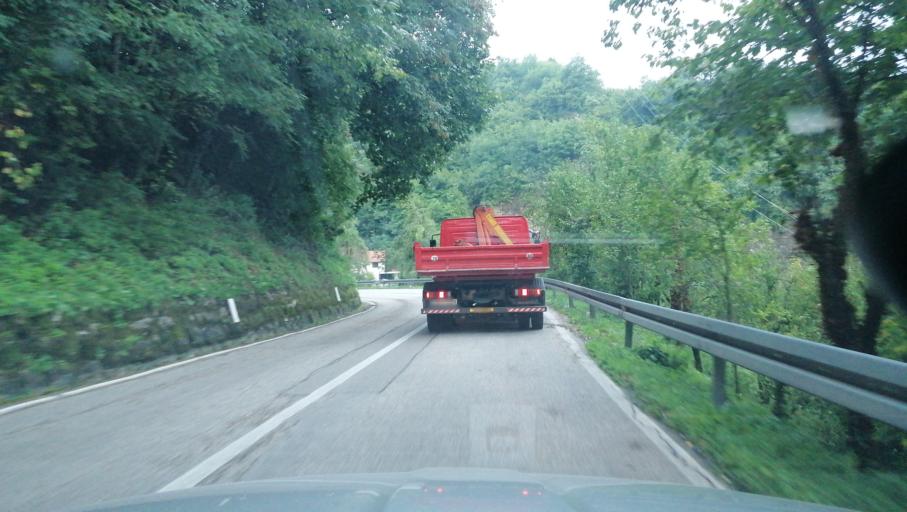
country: BA
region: Federation of Bosnia and Herzegovina
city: Jablanica
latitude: 43.7274
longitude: 17.6870
